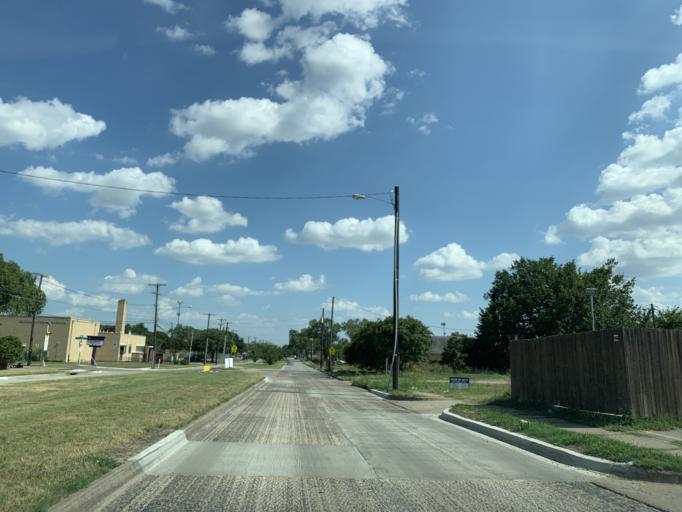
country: US
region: Texas
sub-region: Dallas County
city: Hutchins
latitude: 32.6985
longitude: -96.7749
